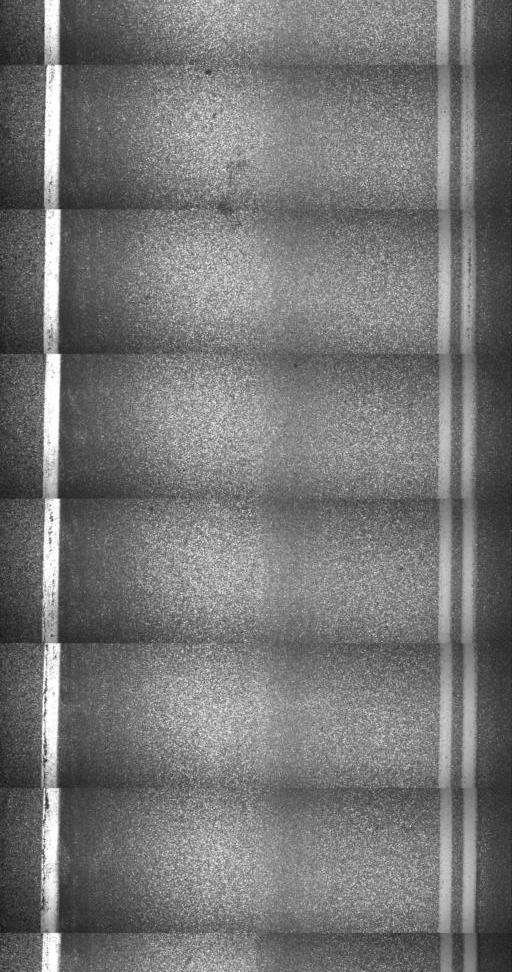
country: US
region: Vermont
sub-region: Washington County
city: Northfield
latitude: 44.0684
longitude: -72.8585
